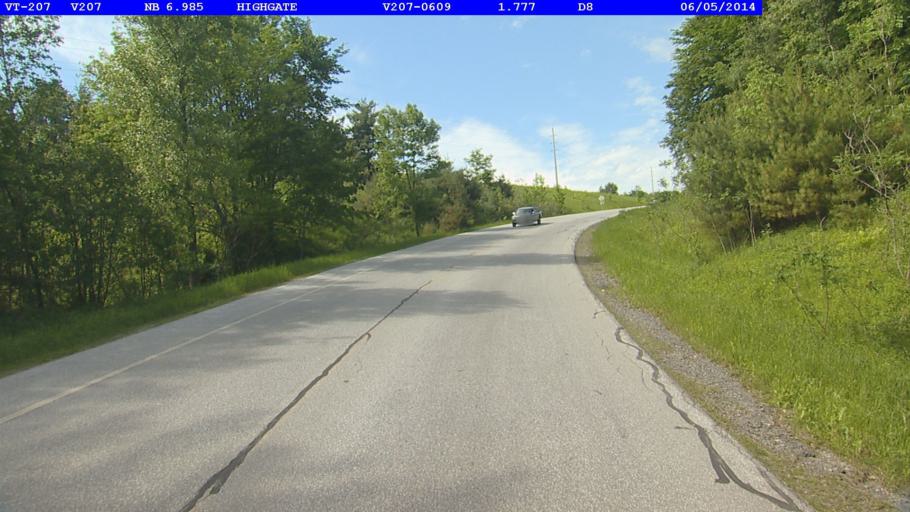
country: US
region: Vermont
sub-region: Franklin County
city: Swanton
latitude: 44.9358
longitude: -73.0501
